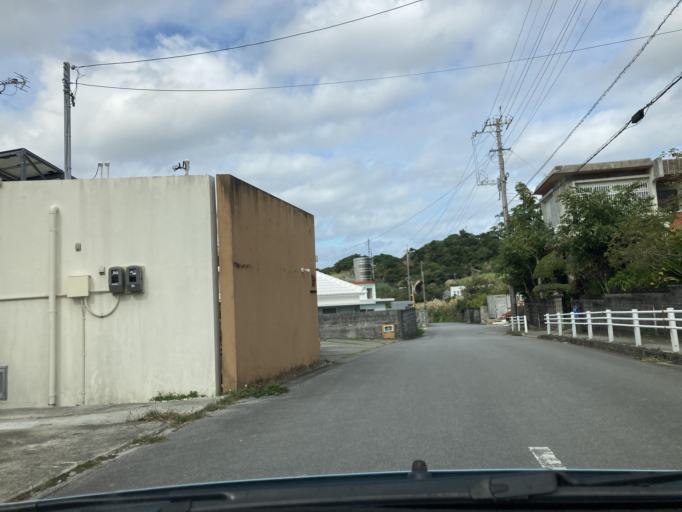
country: JP
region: Okinawa
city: Ginowan
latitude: 26.2102
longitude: 127.7458
